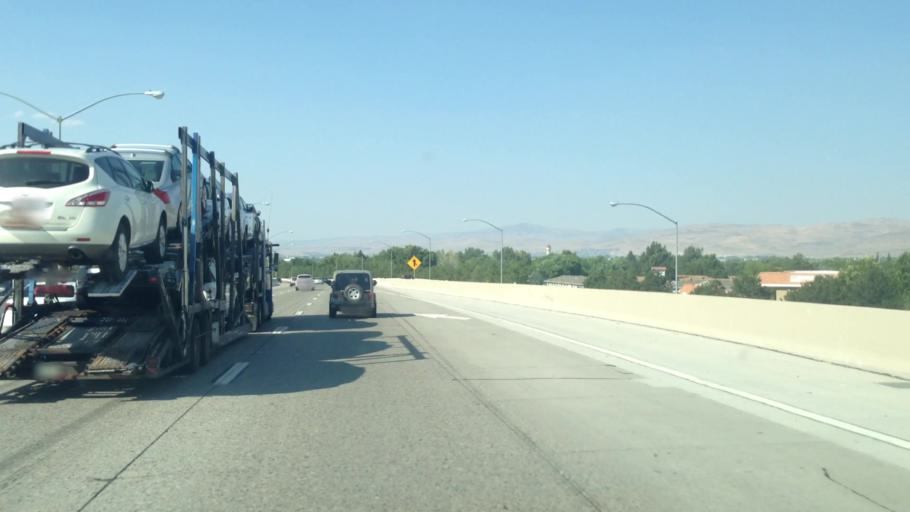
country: US
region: Nevada
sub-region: Washoe County
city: Reno
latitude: 39.4786
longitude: -119.7892
